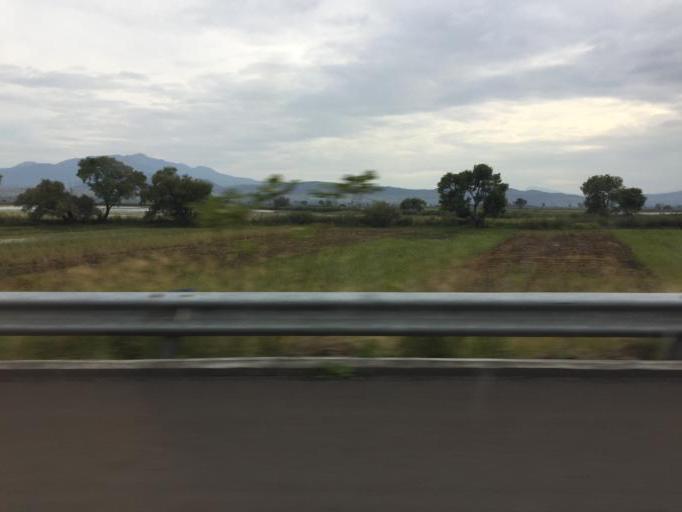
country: MX
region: Mexico
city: Huaniqueo de Morales
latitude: 19.8919
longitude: -101.5346
